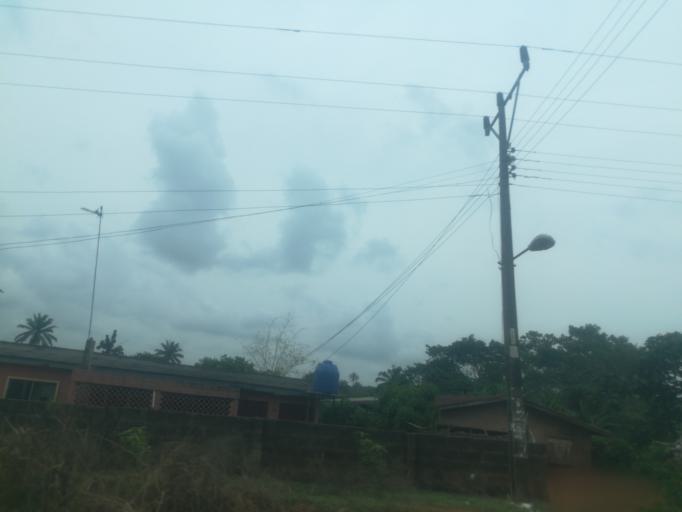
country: NG
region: Ogun
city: Ayetoro
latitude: 7.1110
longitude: 3.1291
